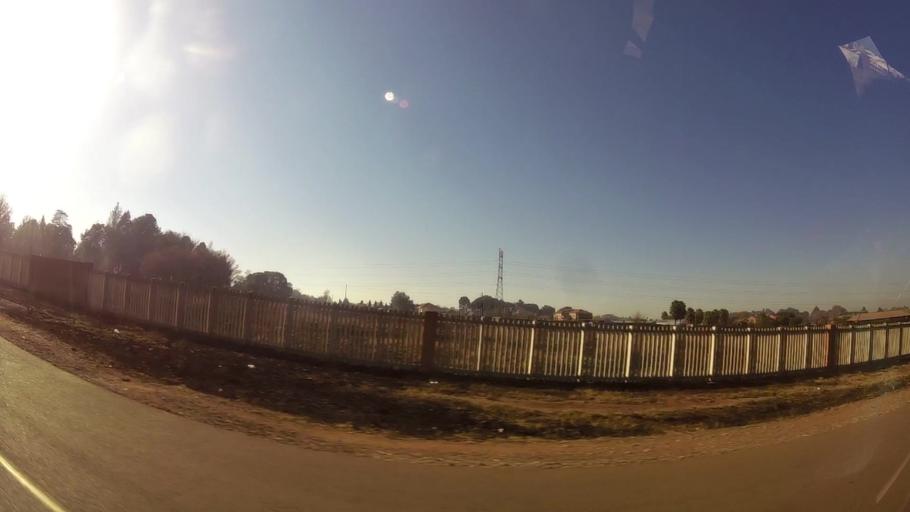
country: ZA
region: Gauteng
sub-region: City of Tshwane Metropolitan Municipality
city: Centurion
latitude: -25.8391
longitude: 28.1108
